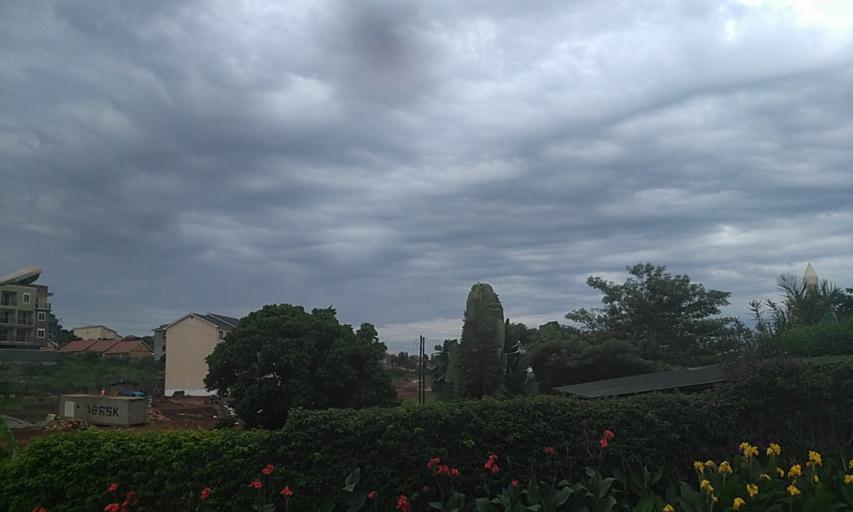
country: UG
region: Central Region
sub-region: Wakiso District
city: Kireka
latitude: 0.3737
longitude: 32.6429
